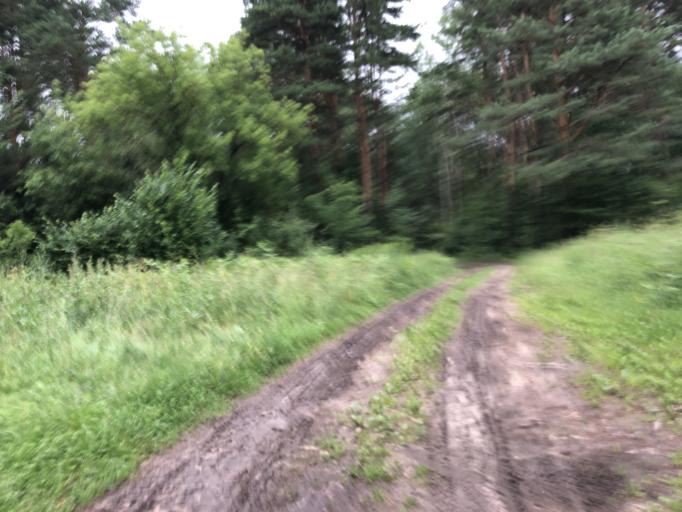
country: RU
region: Tverskaya
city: Rzhev
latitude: 56.2465
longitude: 34.3705
